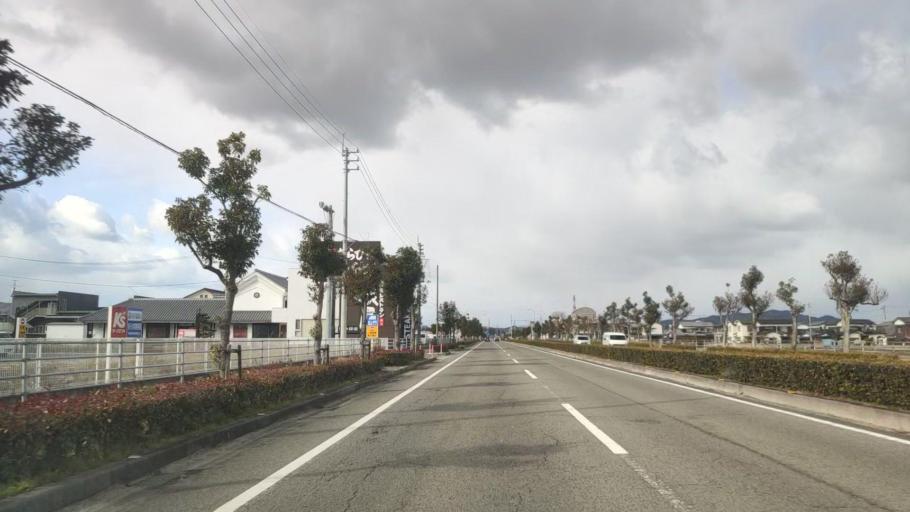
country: JP
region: Ehime
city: Saijo
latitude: 34.0380
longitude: 132.9957
